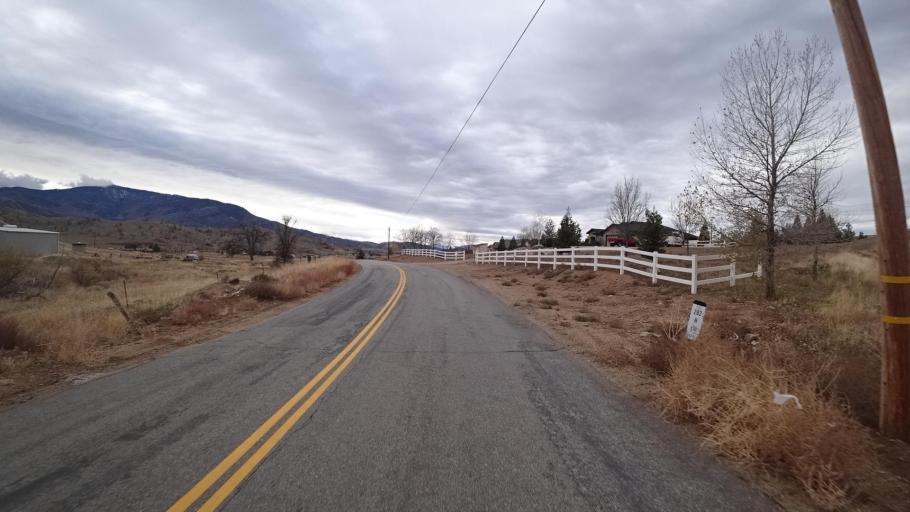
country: US
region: California
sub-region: Kern County
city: Bear Valley Springs
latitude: 35.1333
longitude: -118.5631
